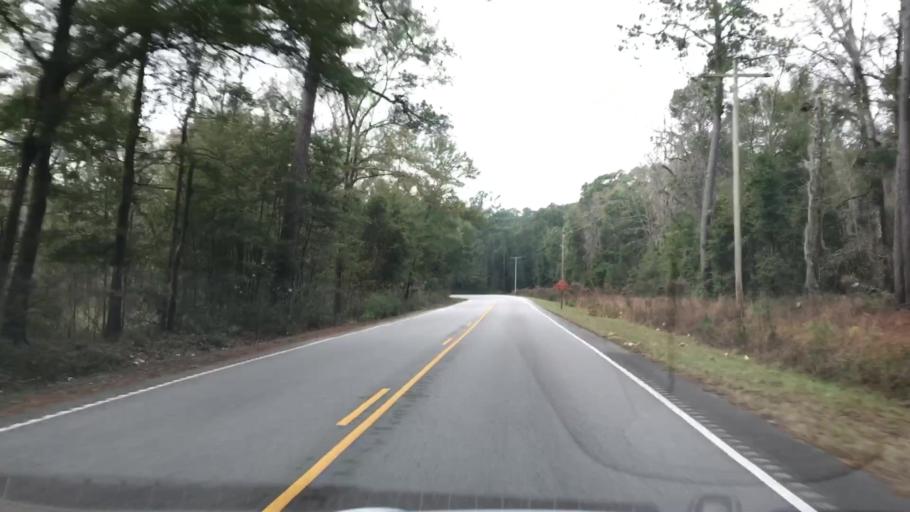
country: US
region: South Carolina
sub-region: Jasper County
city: Ridgeland
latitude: 32.4909
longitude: -80.8870
